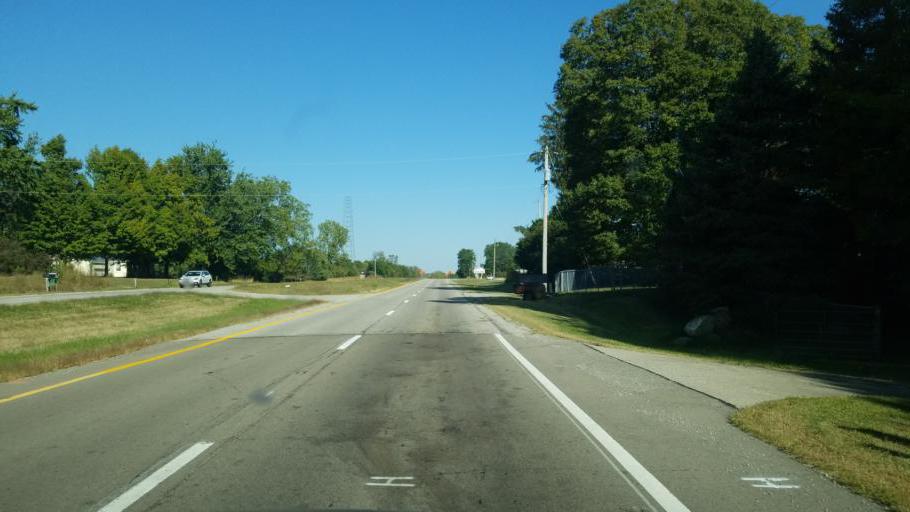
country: US
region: Ohio
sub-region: Madison County
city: Choctaw Lake
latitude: 39.9311
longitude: -83.5396
